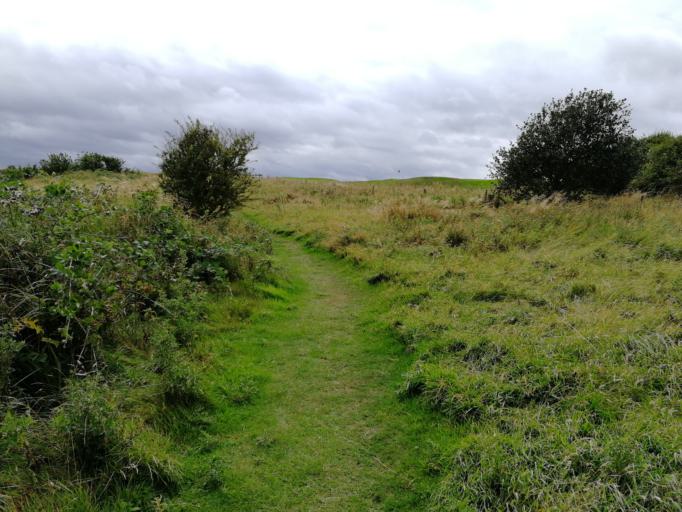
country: GB
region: England
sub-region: North Yorkshire
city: Filey
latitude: 54.2021
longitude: -0.2862
